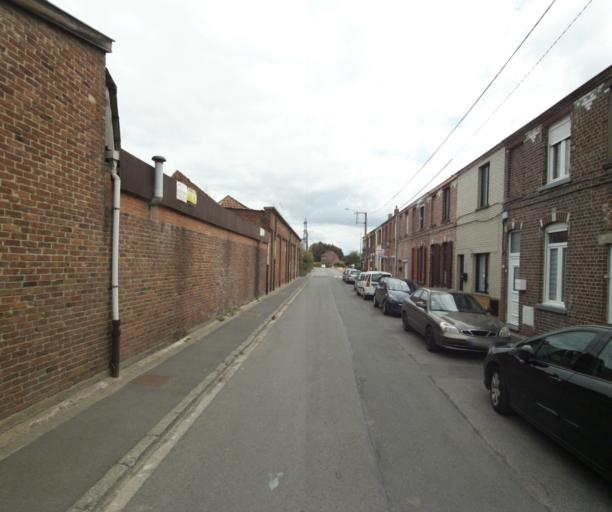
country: FR
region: Nord-Pas-de-Calais
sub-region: Departement du Nord
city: Anstaing
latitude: 50.6089
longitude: 3.1809
